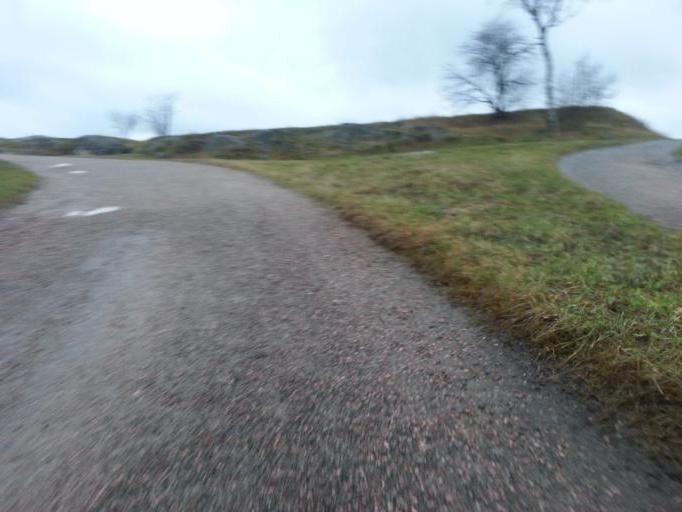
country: FI
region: Uusimaa
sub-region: Helsinki
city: Helsinki
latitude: 60.1401
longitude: 24.9866
